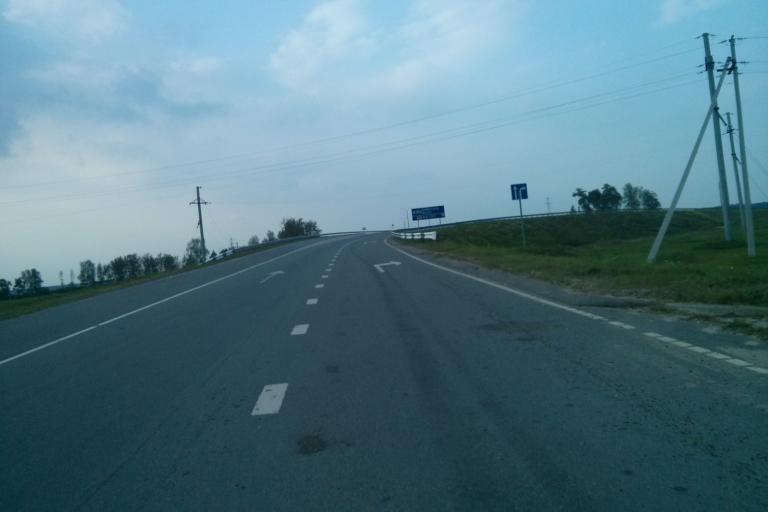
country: BY
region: Minsk
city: Chervyen'
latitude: 53.7209
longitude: 28.3960
